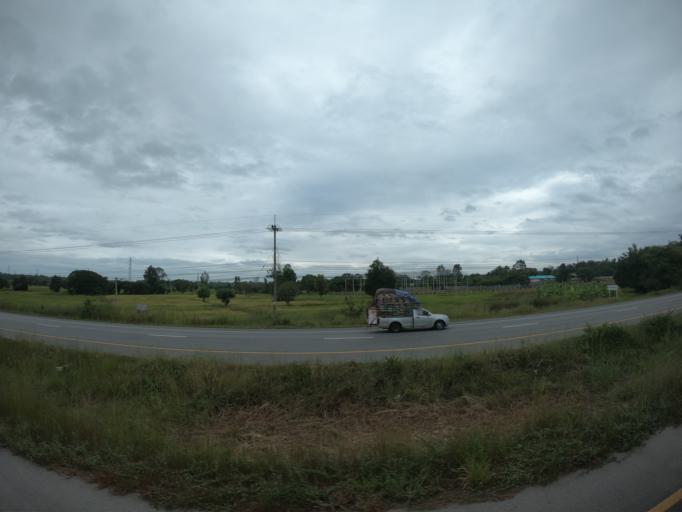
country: TH
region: Roi Et
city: Changhan
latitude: 16.1026
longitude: 103.5228
